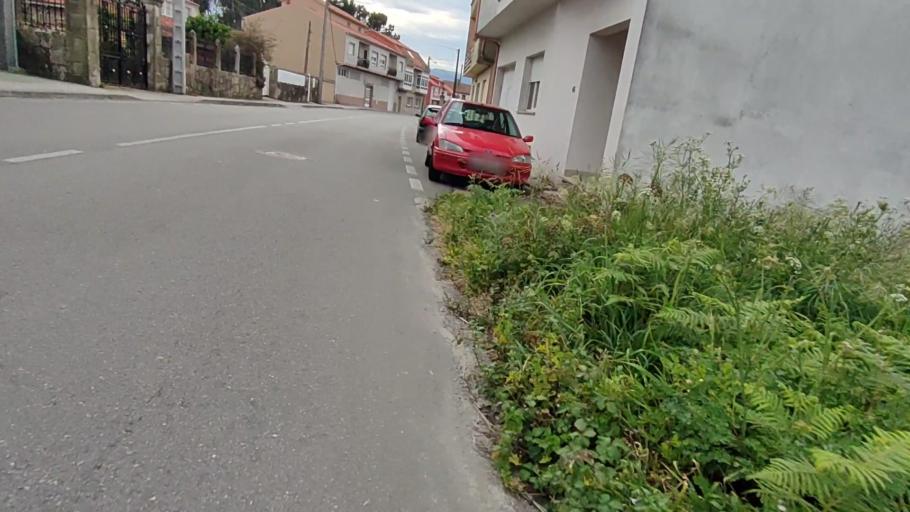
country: ES
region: Galicia
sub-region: Provincia da Coruna
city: Boiro
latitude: 42.6347
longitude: -8.8695
